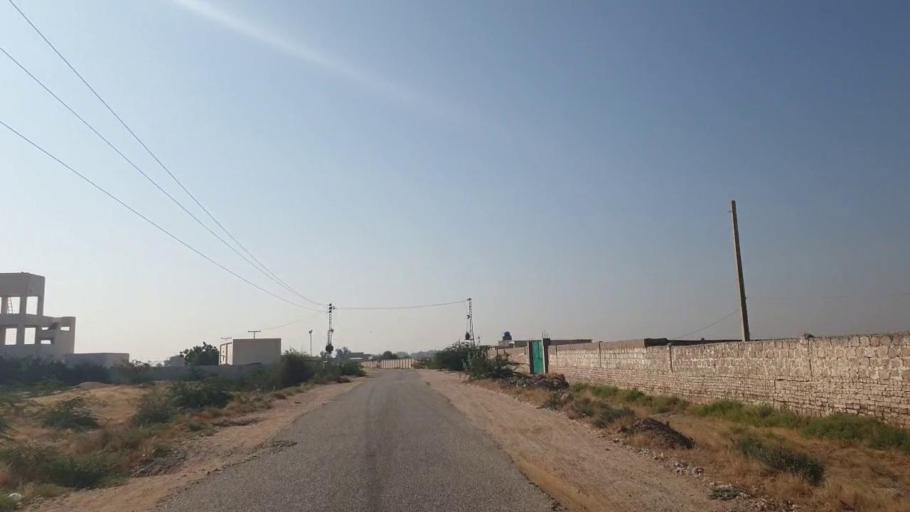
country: PK
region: Sindh
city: Thatta
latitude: 25.1605
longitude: 67.7736
